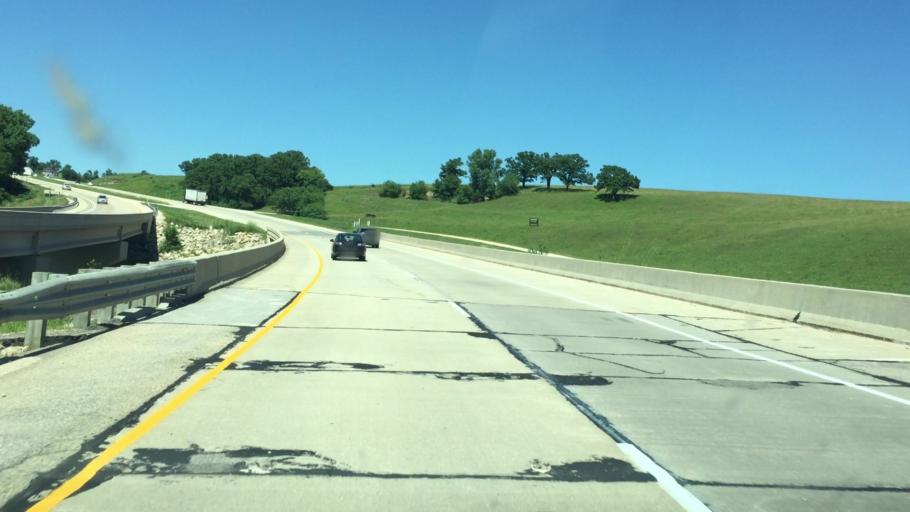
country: US
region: Wisconsin
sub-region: Iowa County
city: Mineral Point
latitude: 42.8116
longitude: -90.2585
